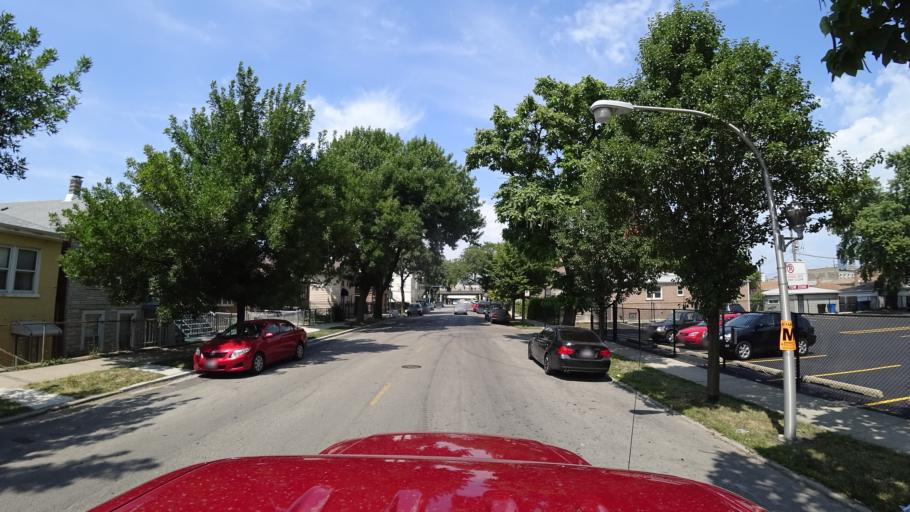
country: US
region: Illinois
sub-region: Cook County
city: Chicago
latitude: 41.8425
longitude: -87.6533
